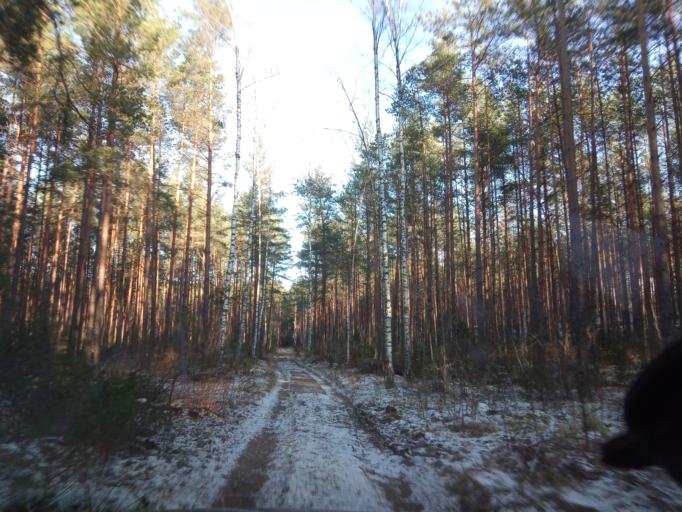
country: LT
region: Alytaus apskritis
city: Druskininkai
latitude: 53.9502
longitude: 23.8811
